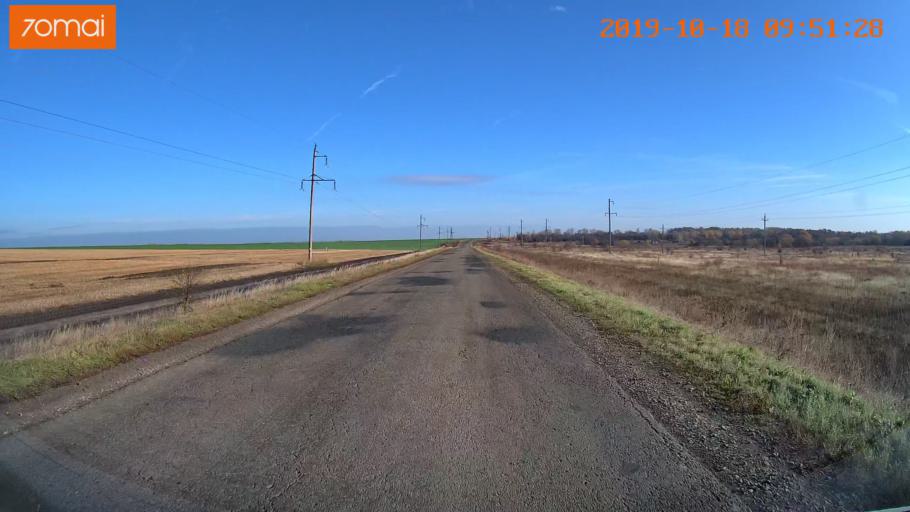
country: RU
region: Tula
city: Kazachka
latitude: 53.3411
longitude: 38.2931
